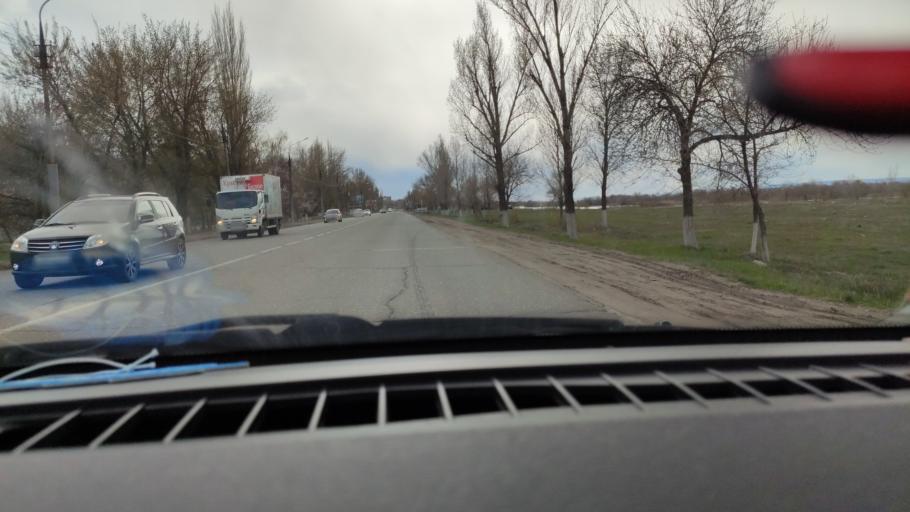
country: RU
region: Saratov
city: Engel's
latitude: 51.4549
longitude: 46.0860
